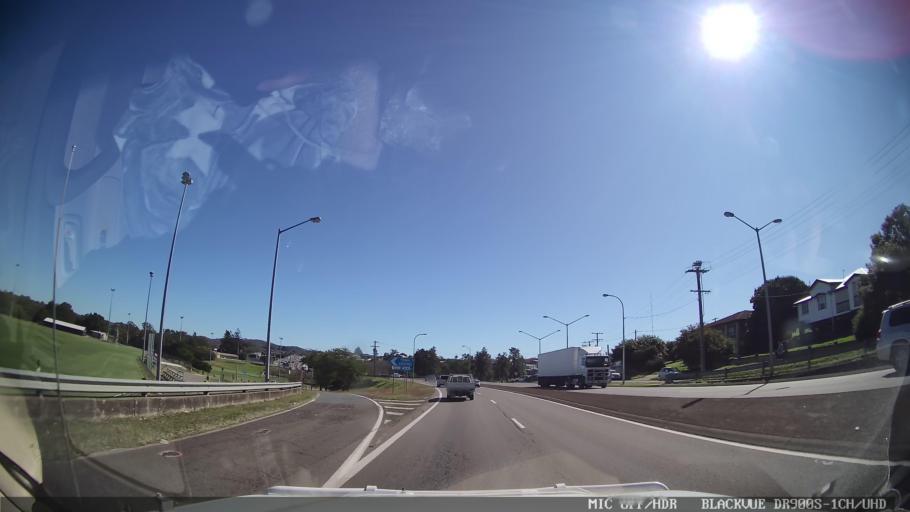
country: AU
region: Queensland
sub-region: Gympie Regional Council
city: Gympie
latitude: -26.1949
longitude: 152.6615
